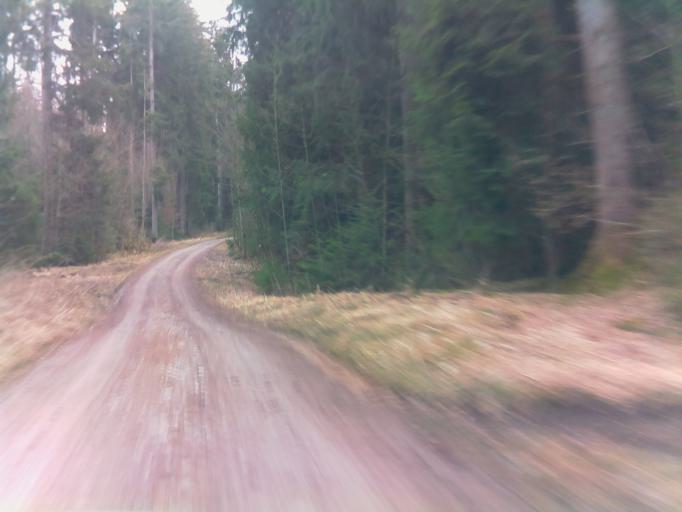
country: DE
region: Bavaria
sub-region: Upper Bavaria
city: Ingenried
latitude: 47.8488
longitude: 10.7946
